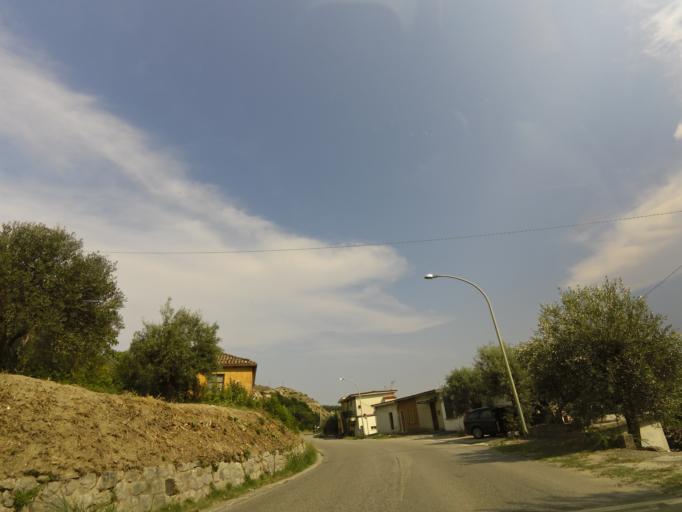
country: IT
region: Calabria
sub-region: Provincia di Catanzaro
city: Guardavalle
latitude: 38.4651
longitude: 16.5106
